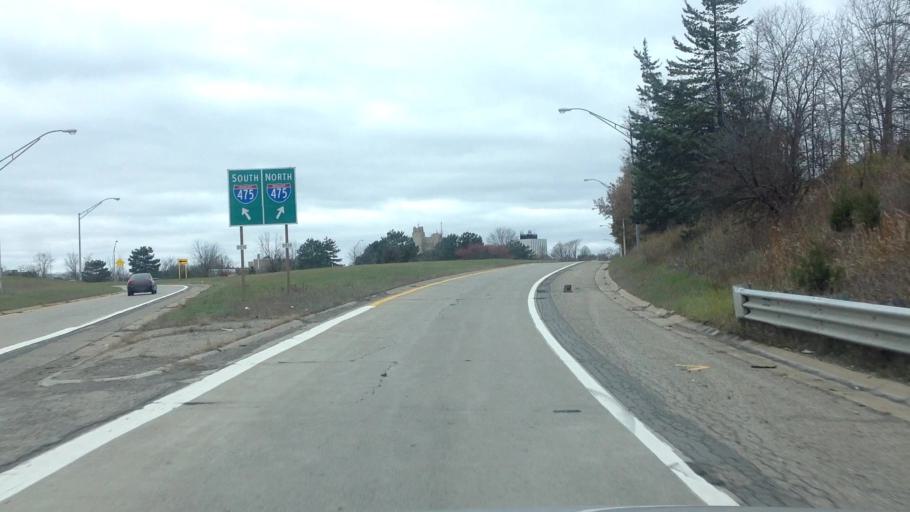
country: US
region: Michigan
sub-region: Genesee County
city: Flint
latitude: 43.0112
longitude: -83.6760
